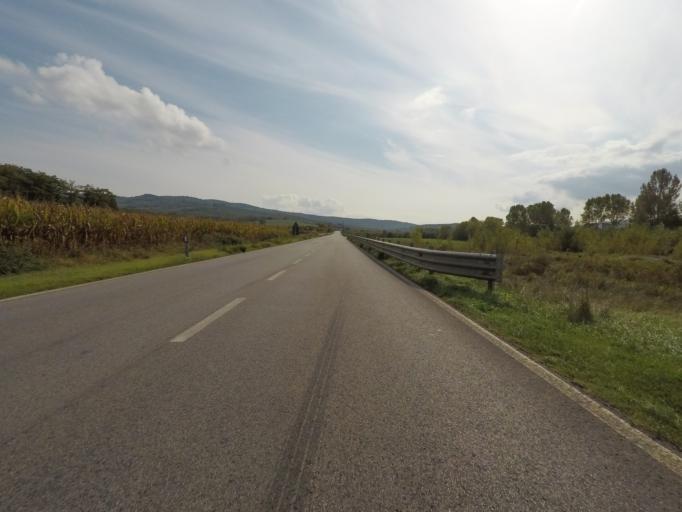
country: IT
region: Tuscany
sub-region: Provincia di Siena
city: Rosia
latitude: 43.1703
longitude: 11.2822
